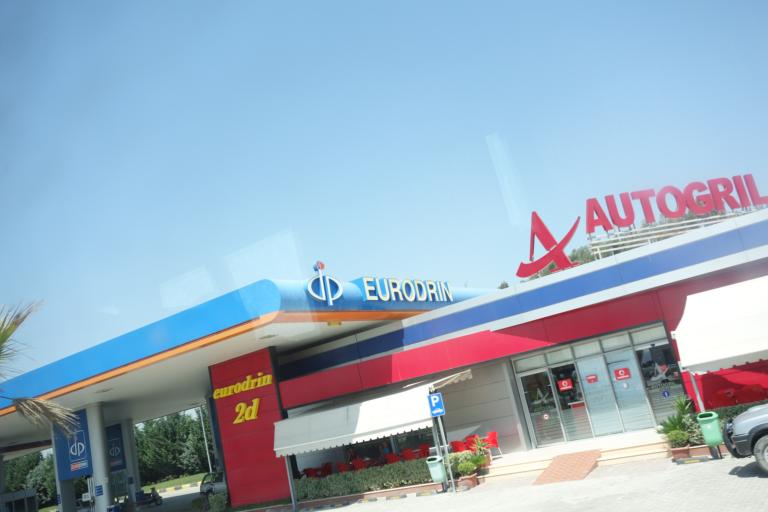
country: AL
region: Tirane
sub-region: Rrethi i Kavajes
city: Luzi i Vogel
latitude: 41.1449
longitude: 19.5903
